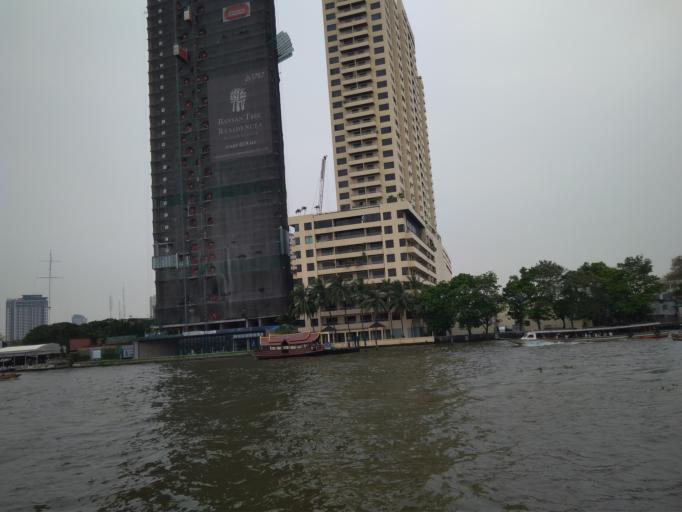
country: TH
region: Bangkok
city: Khlong San
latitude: 13.7374
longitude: 100.5060
